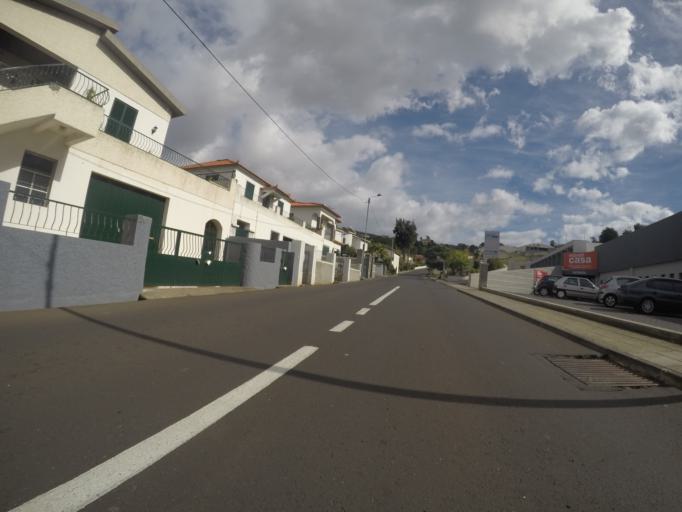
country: PT
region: Madeira
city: Camara de Lobos
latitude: 32.6498
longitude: -16.9571
